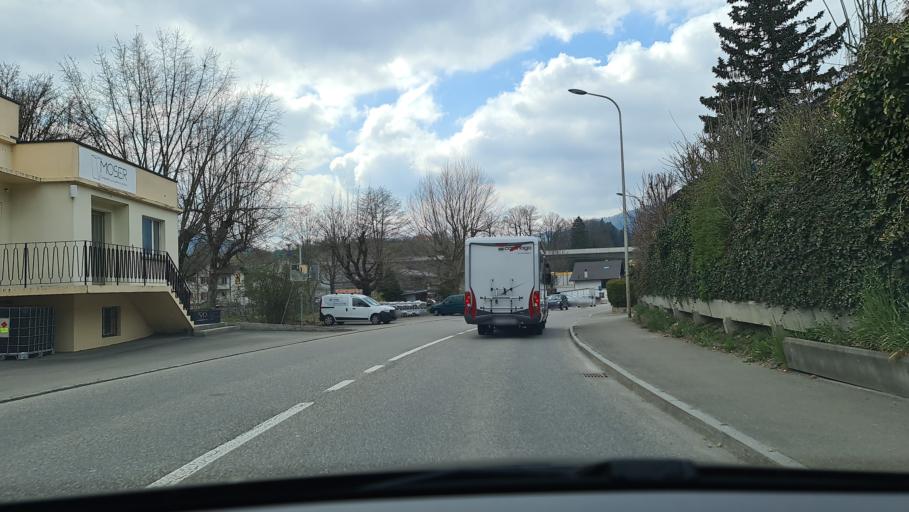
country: CH
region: Bern
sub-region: Jura bernois
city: Moutier
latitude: 47.2786
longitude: 7.3956
